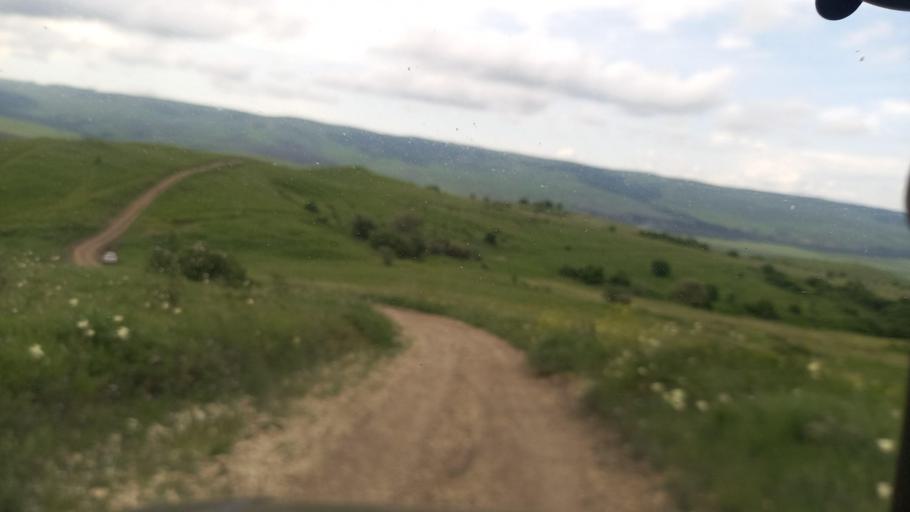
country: RU
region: Krasnodarskiy
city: Peredovaya
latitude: 44.0619
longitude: 41.3627
